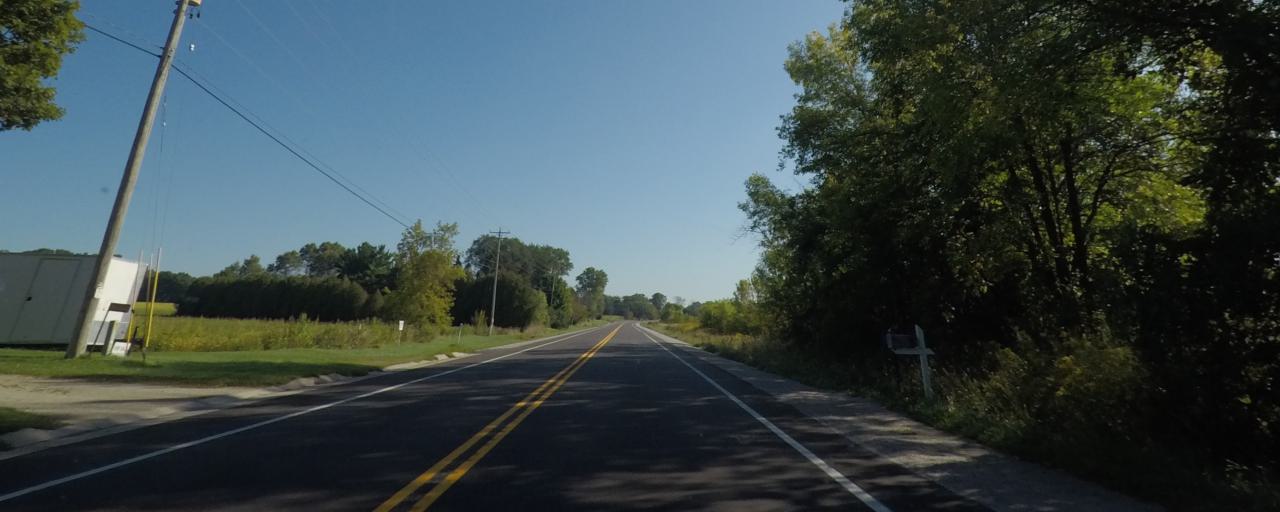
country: US
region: Wisconsin
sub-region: Jefferson County
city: Jefferson
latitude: 43.0132
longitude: -88.7513
